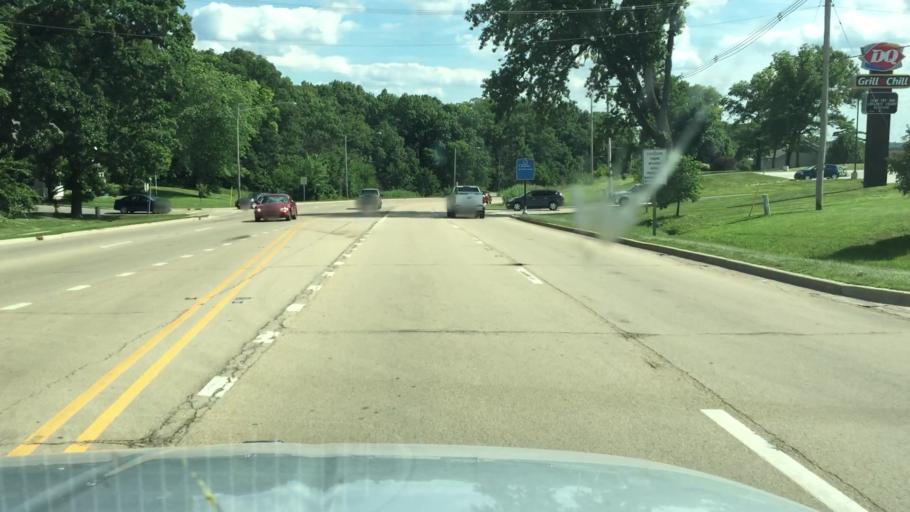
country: US
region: Illinois
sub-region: LaSalle County
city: Ottawa
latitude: 41.3694
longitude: -88.8358
